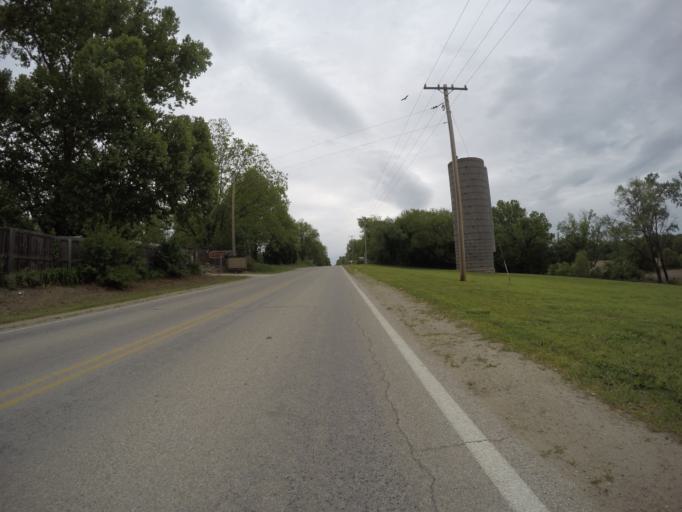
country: US
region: Kansas
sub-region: Riley County
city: Manhattan
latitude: 39.1965
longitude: -96.4588
